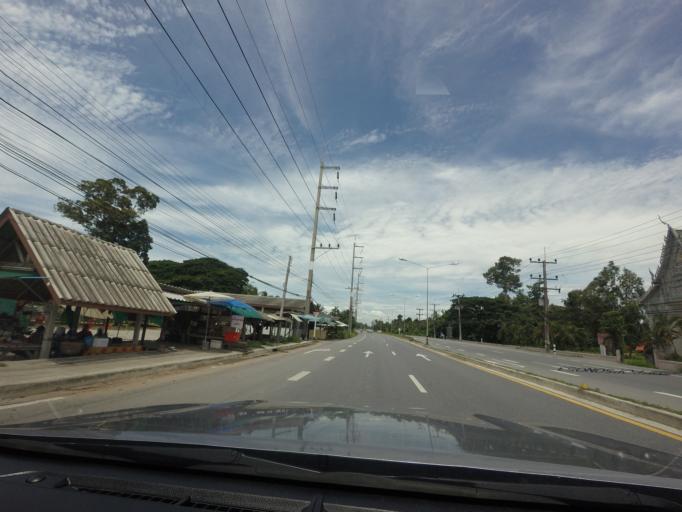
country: TH
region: Songkhla
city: Krasae Sin
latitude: 7.6127
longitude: 100.3980
